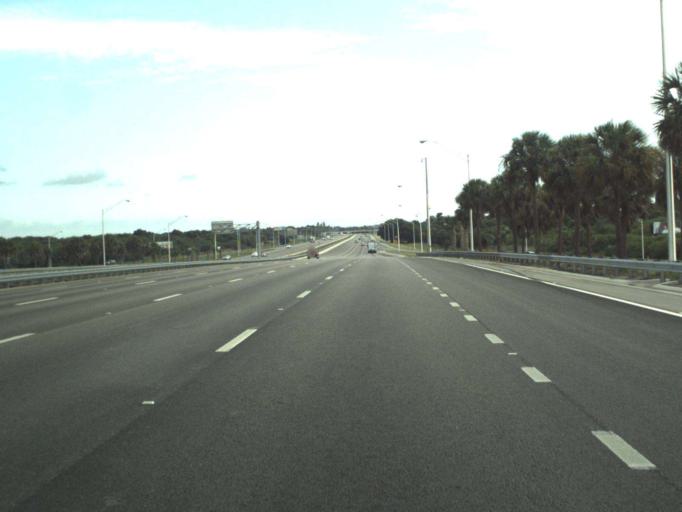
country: US
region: Florida
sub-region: Saint Lucie County
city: Fort Pierce South
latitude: 27.4168
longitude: -80.3882
